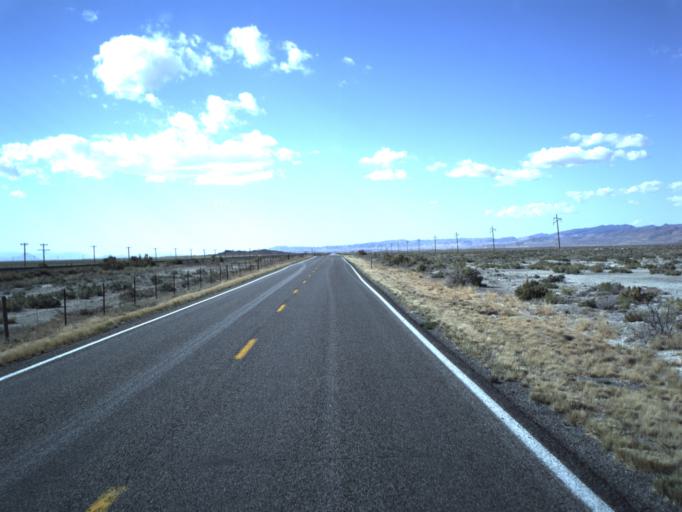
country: US
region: Utah
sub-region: Millard County
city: Delta
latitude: 39.1804
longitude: -112.7003
